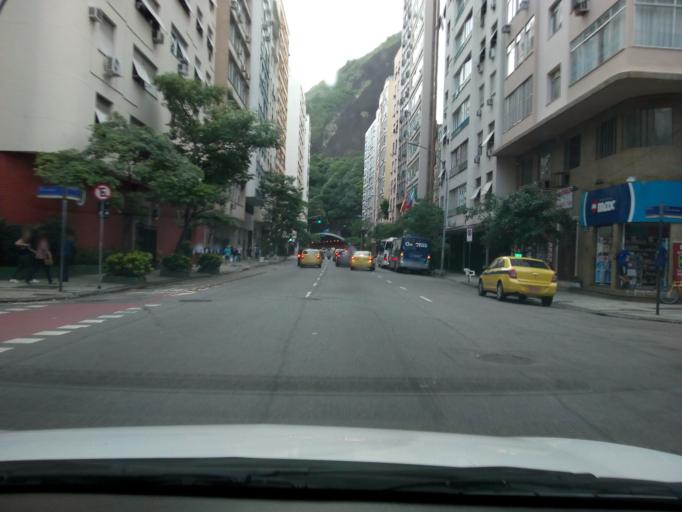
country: BR
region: Rio de Janeiro
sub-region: Rio De Janeiro
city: Rio de Janeiro
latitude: -22.9684
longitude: -43.1884
